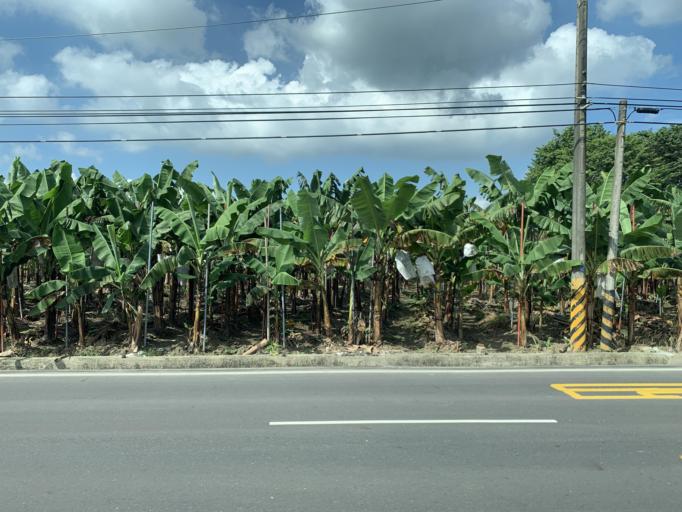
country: TW
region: Taiwan
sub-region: Pingtung
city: Pingtung
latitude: 22.8738
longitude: 120.4977
